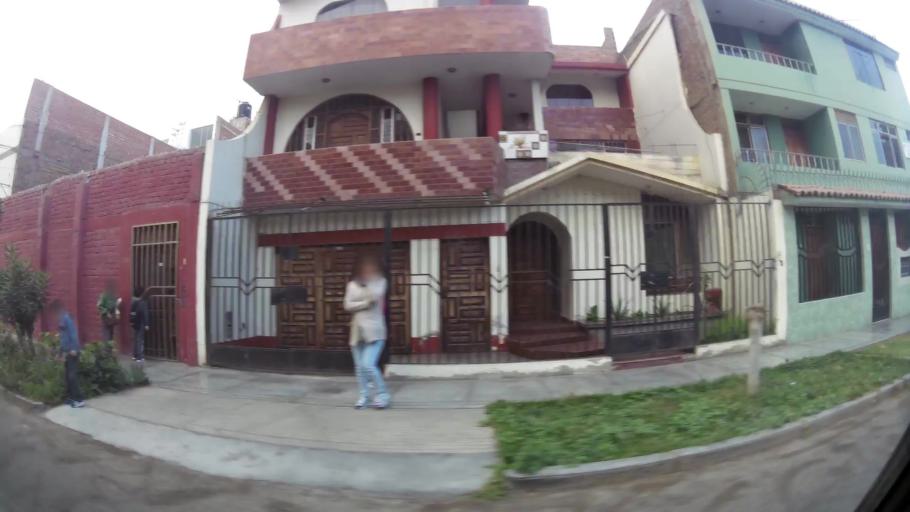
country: PE
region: La Libertad
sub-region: Provincia de Trujillo
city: Trujillo
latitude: -8.0962
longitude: -79.0252
